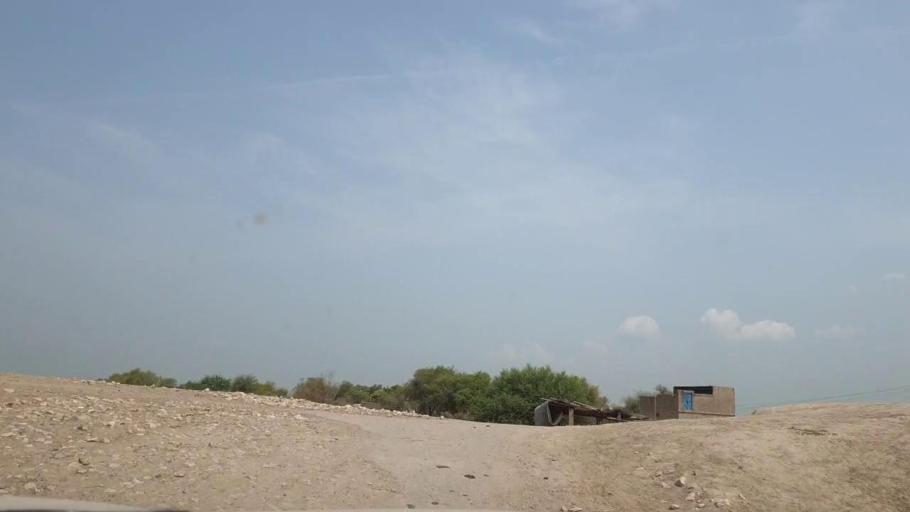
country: PK
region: Sindh
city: Dokri
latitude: 27.4061
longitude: 68.2435
